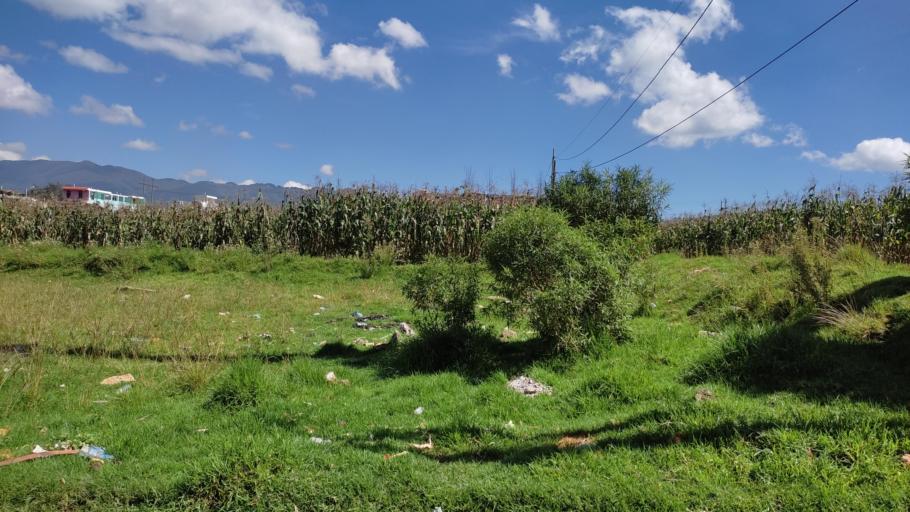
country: GT
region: Quetzaltenango
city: Quetzaltenango
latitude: 14.8573
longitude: -91.5245
